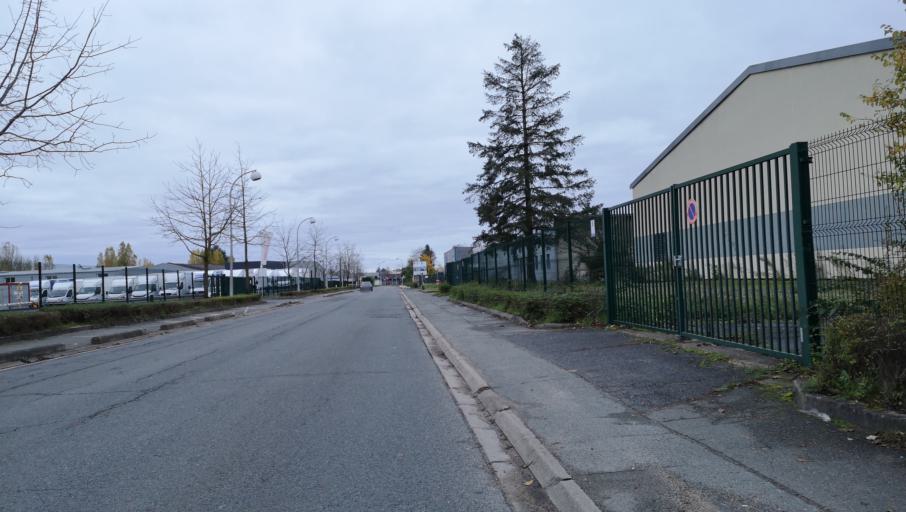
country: FR
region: Centre
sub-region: Departement du Loiret
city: Semoy
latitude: 47.9192
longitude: 1.9469
